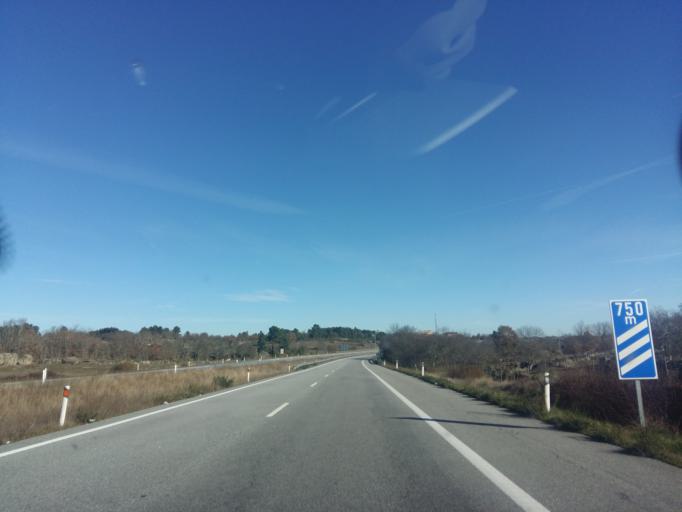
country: PT
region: Guarda
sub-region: Guarda
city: Sequeira
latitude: 40.6042
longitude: -7.0810
